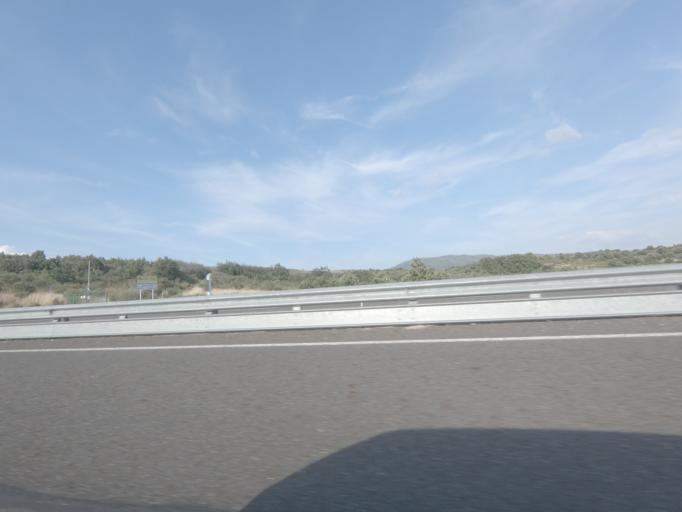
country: ES
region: Galicia
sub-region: Provincia de Ourense
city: Oimbra
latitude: 41.8472
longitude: -7.4125
